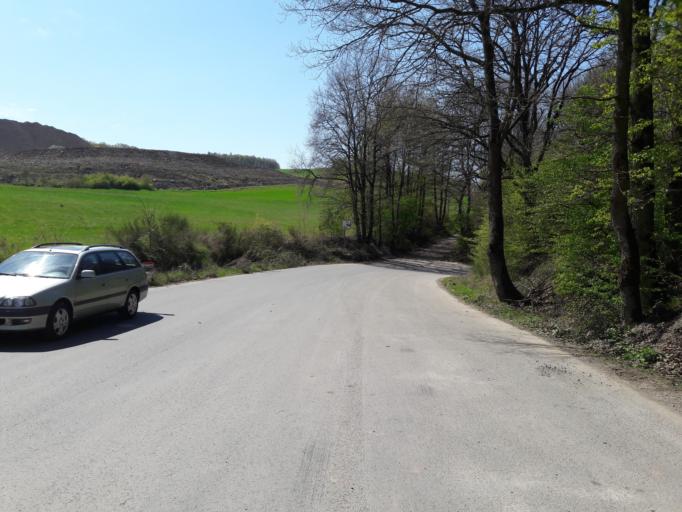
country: DE
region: Rheinland-Pfalz
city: Pfeffelbach
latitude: 49.5470
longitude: 7.3437
